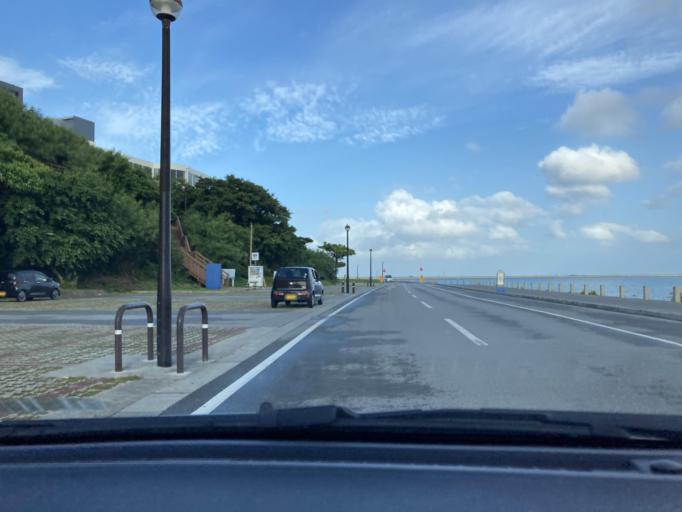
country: JP
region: Okinawa
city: Tomigusuku
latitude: 26.1767
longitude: 127.6425
